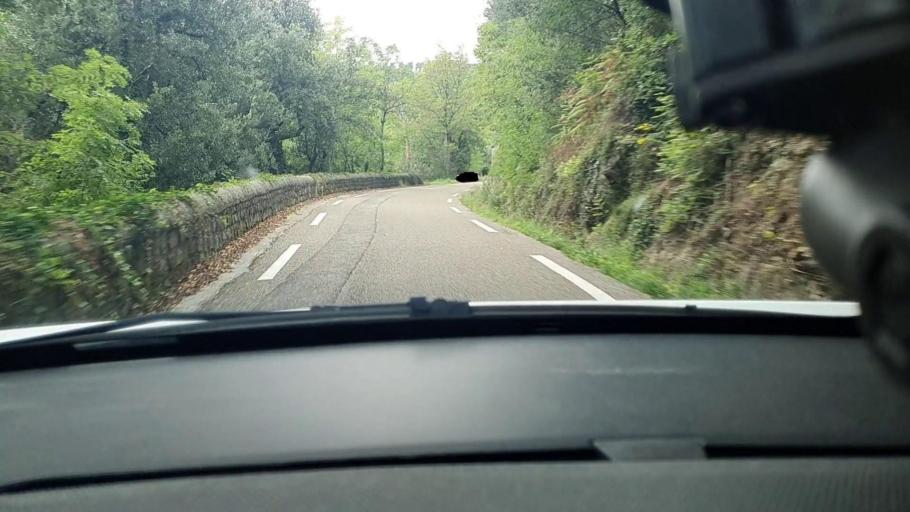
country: FR
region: Languedoc-Roussillon
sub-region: Departement du Gard
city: Branoux-les-Taillades
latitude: 44.3046
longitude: 3.9923
